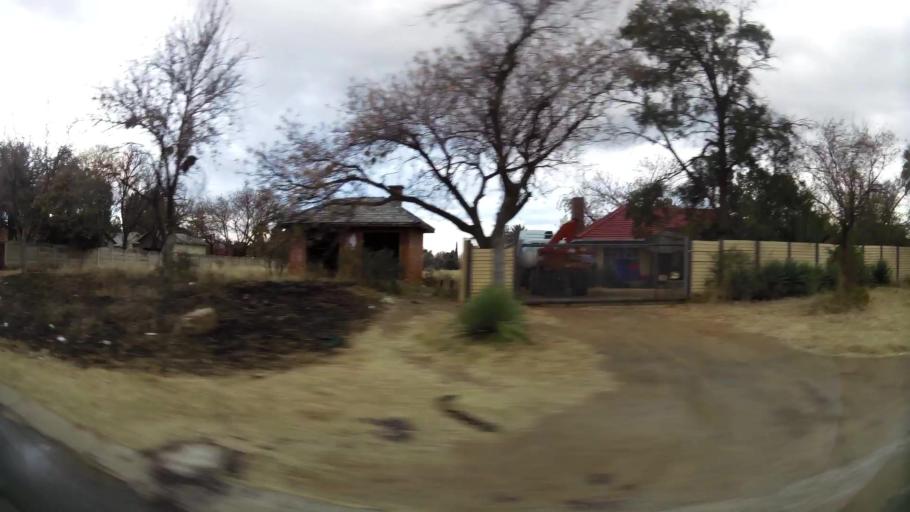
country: ZA
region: Orange Free State
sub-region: Lejweleputswa District Municipality
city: Welkom
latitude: -27.9617
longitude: 26.7219
